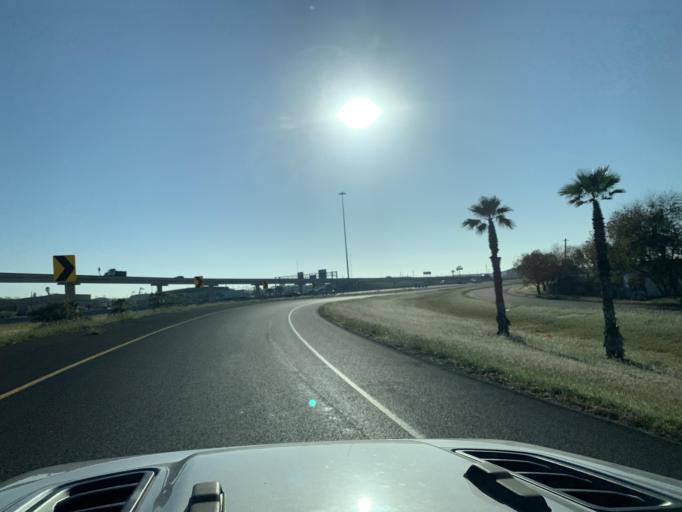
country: US
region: Texas
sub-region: Nueces County
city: Corpus Christi
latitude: 27.7816
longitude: -97.4713
